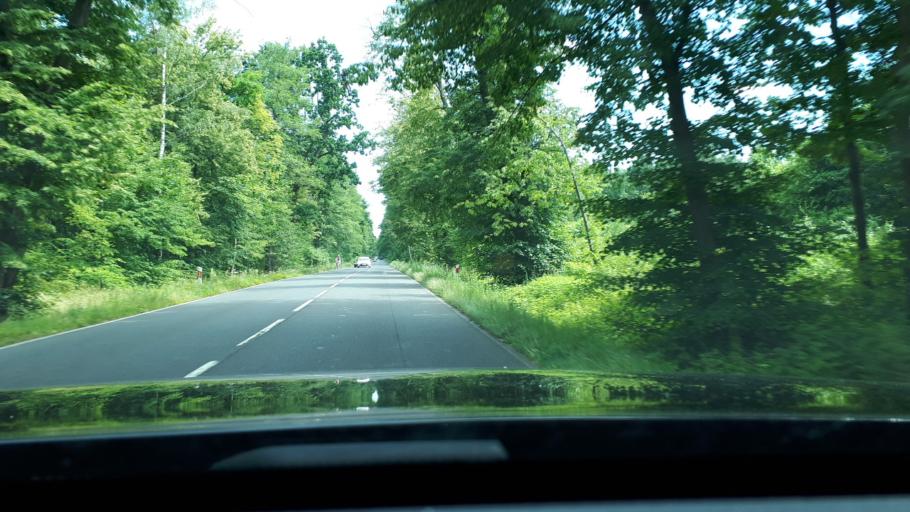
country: PL
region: Lodz Voivodeship
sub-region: powiat Lowicki
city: Bobrowniki
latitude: 52.0727
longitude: 20.0434
